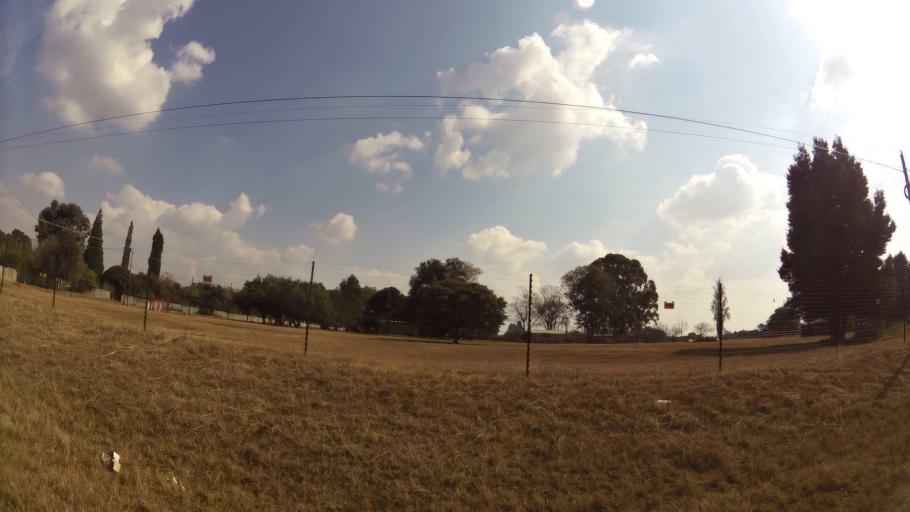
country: ZA
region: Mpumalanga
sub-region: Nkangala District Municipality
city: Delmas
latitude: -26.1738
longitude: 28.5442
